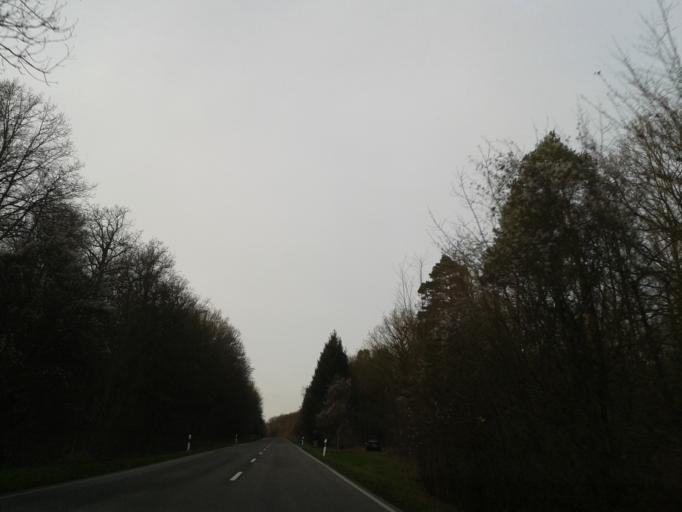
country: DE
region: Bavaria
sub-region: Regierungsbezirk Unterfranken
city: Wonfurt
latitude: 50.0355
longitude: 10.4338
